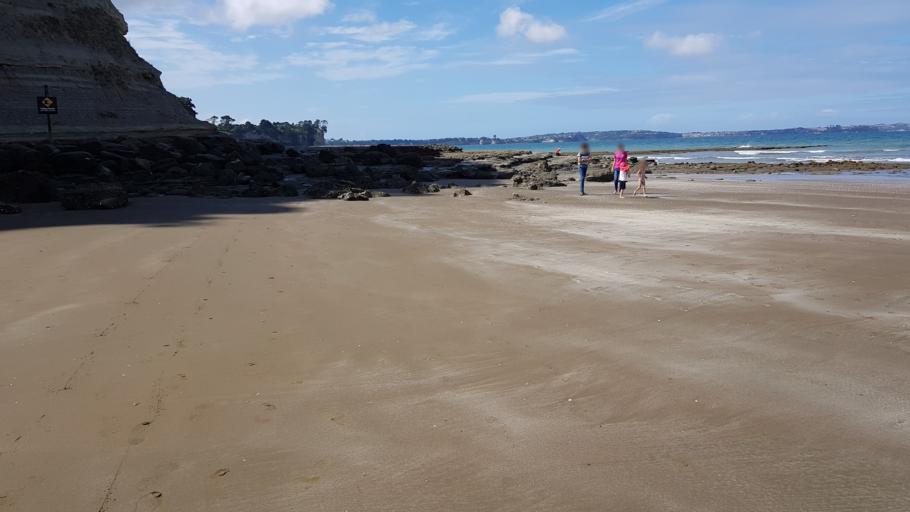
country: NZ
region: Auckland
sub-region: Auckland
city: Rothesay Bay
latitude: -36.6773
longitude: 174.7485
